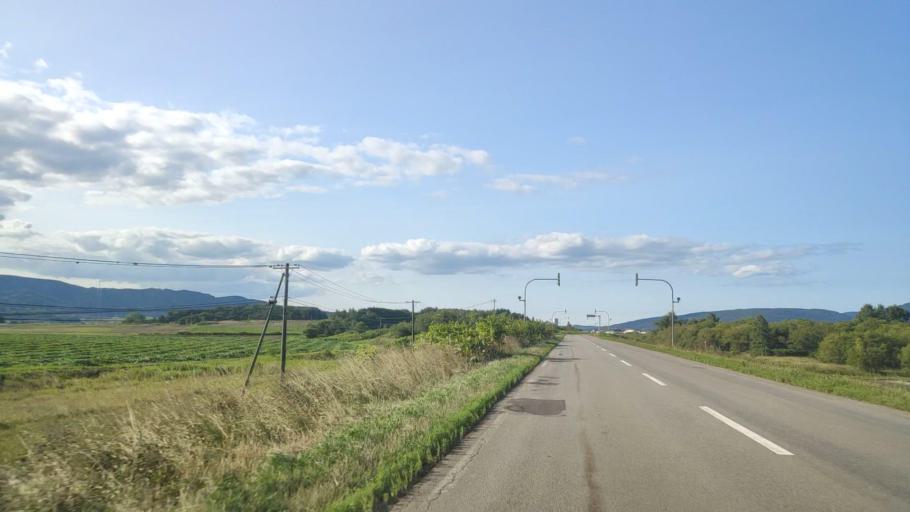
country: JP
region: Hokkaido
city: Nayoro
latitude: 44.8085
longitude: 142.0665
